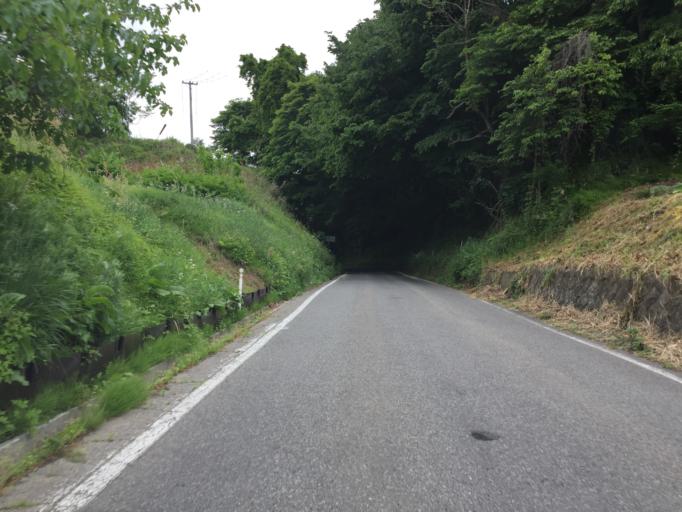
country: JP
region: Fukushima
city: Miharu
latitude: 37.4577
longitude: 140.4706
